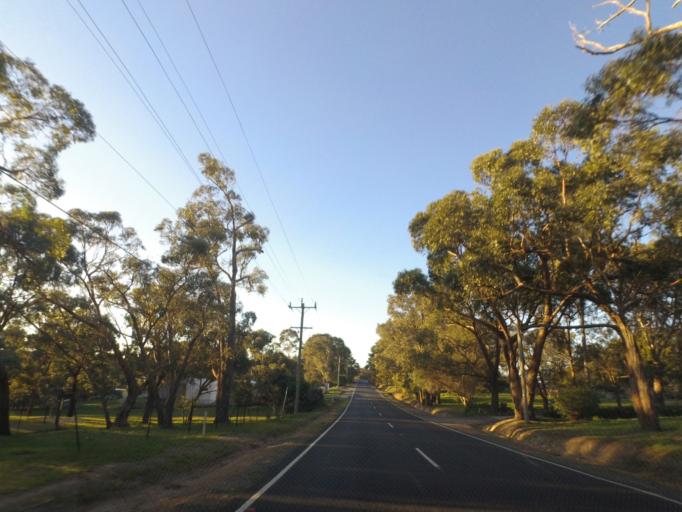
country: AU
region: Victoria
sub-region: Manningham
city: Park Orchards
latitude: -37.7652
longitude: 145.2185
